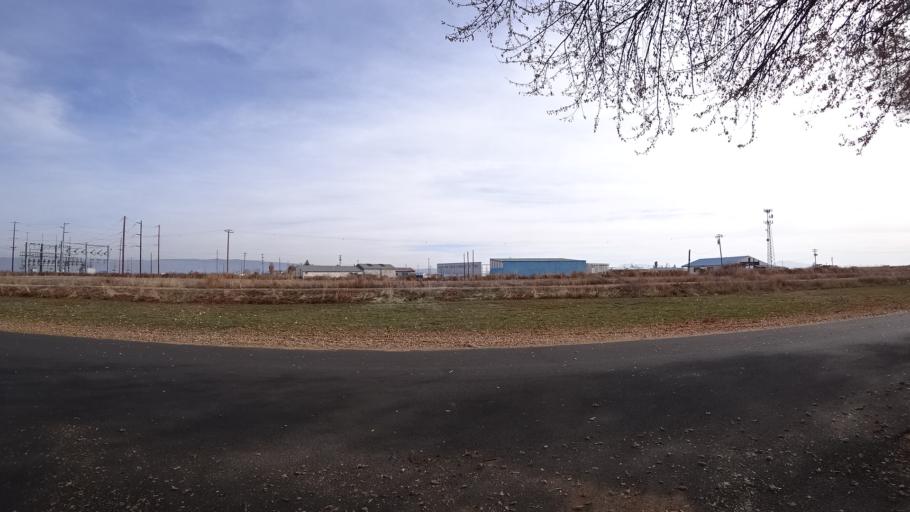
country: US
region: California
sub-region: Siskiyou County
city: Tulelake
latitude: 41.9524
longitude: -121.4724
